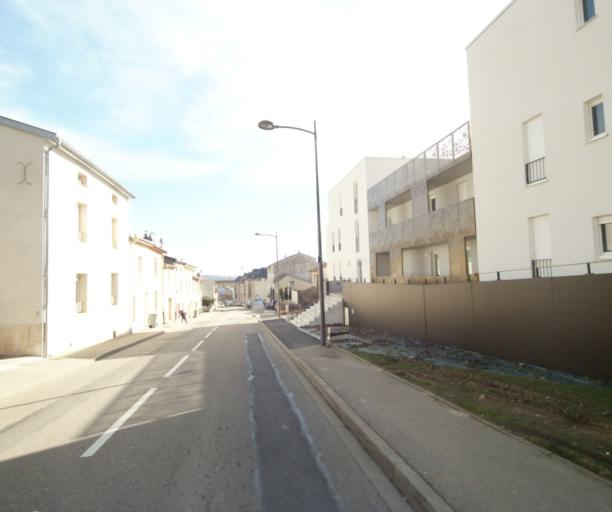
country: FR
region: Lorraine
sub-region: Departement de Meurthe-et-Moselle
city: Maxeville
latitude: 48.7132
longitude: 6.1582
